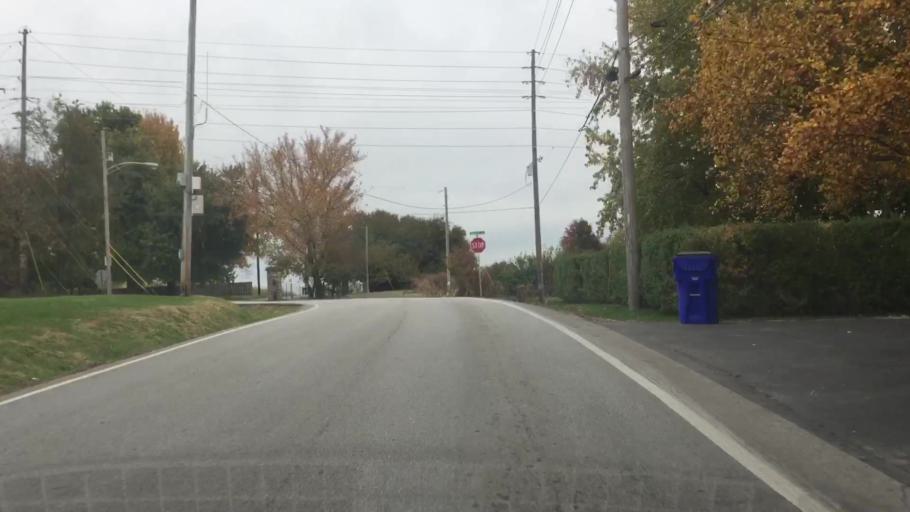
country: US
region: Missouri
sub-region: Cass County
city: Belton
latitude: 38.7990
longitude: -94.5138
